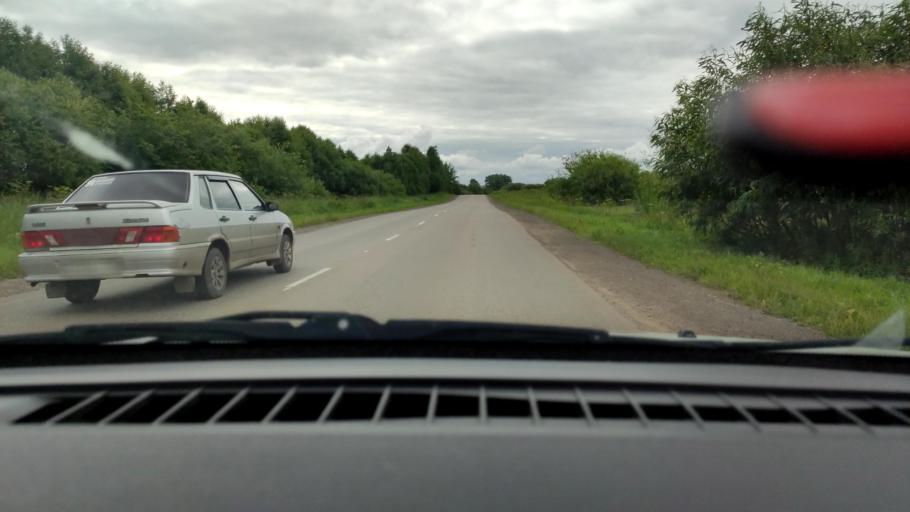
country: RU
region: Perm
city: Chaykovskaya
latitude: 58.1206
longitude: 55.5698
